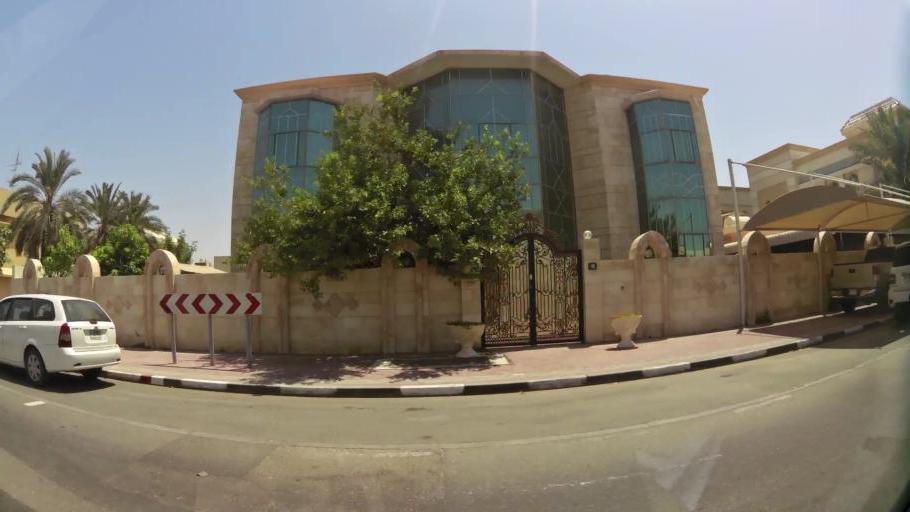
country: AE
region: Ash Shariqah
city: Sharjah
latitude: 25.2960
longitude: 55.3415
